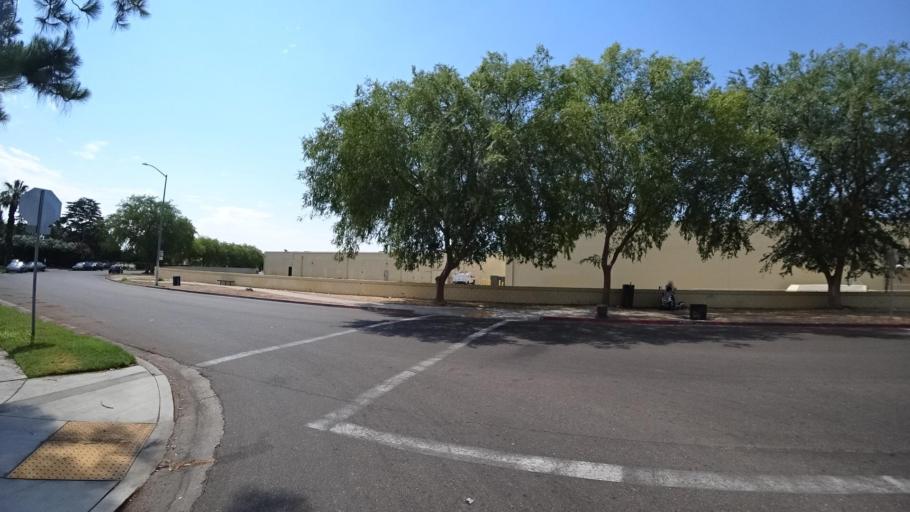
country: US
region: California
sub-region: Fresno County
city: Sunnyside
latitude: 36.7385
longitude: -119.6969
